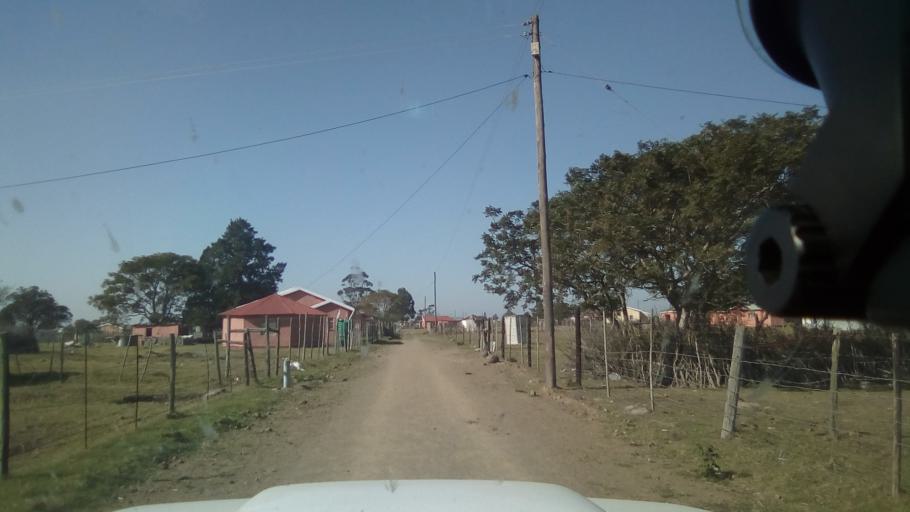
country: ZA
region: Eastern Cape
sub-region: Buffalo City Metropolitan Municipality
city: Bhisho
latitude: -32.9401
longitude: 27.3308
